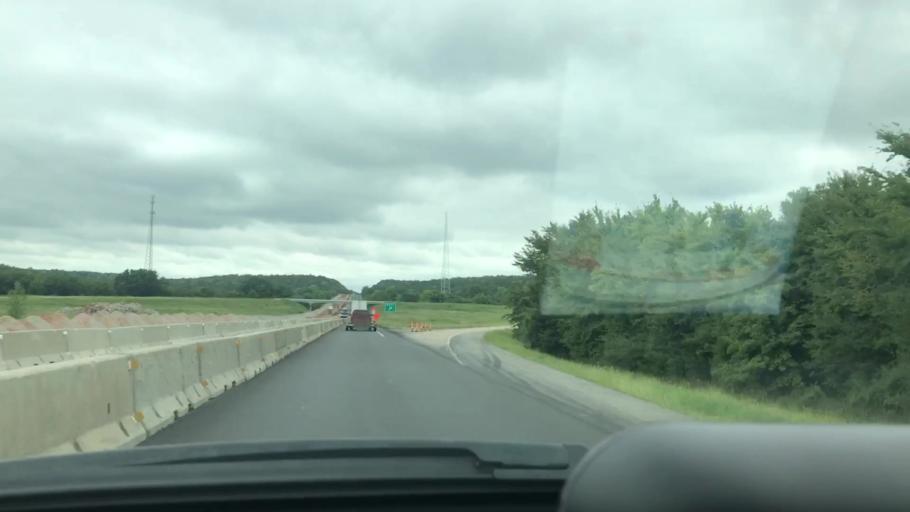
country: US
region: Oklahoma
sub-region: McIntosh County
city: Eufaula
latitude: 35.2588
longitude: -95.5878
